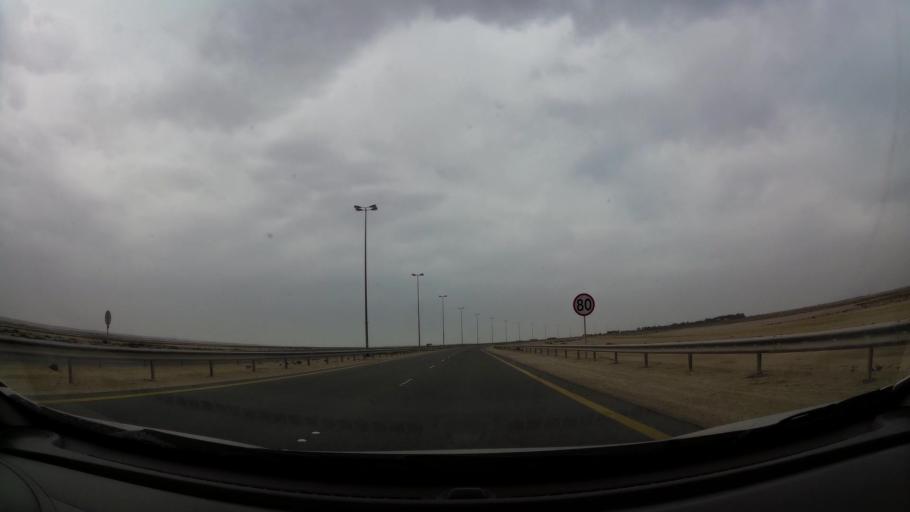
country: BH
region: Central Governorate
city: Dar Kulayb
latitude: 26.0013
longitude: 50.4849
